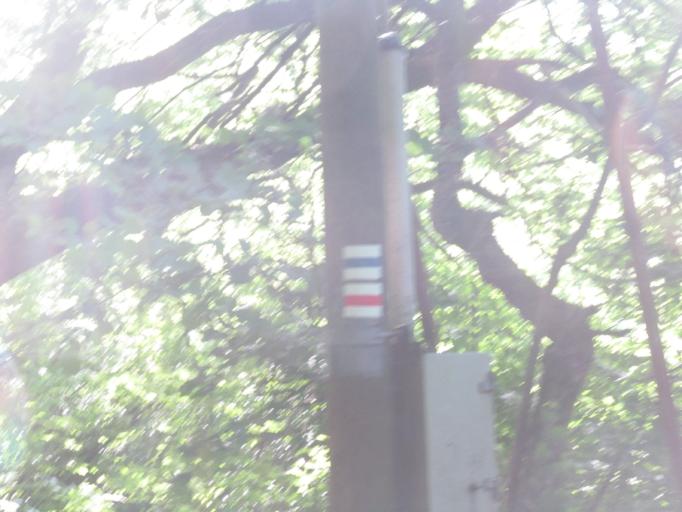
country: HU
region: Borsod-Abauj-Zemplen
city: Gonc
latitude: 48.5440
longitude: 21.4589
